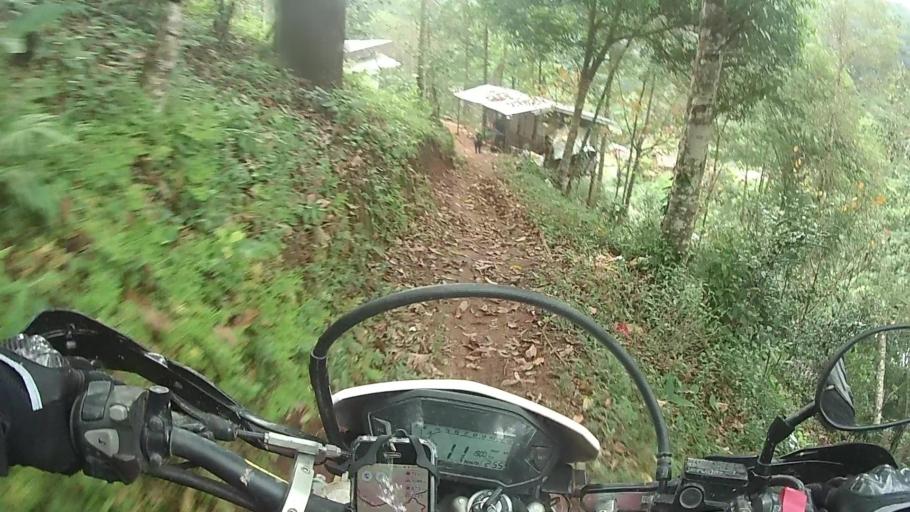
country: TH
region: Chiang Mai
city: Mae On
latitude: 18.9190
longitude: 99.3589
